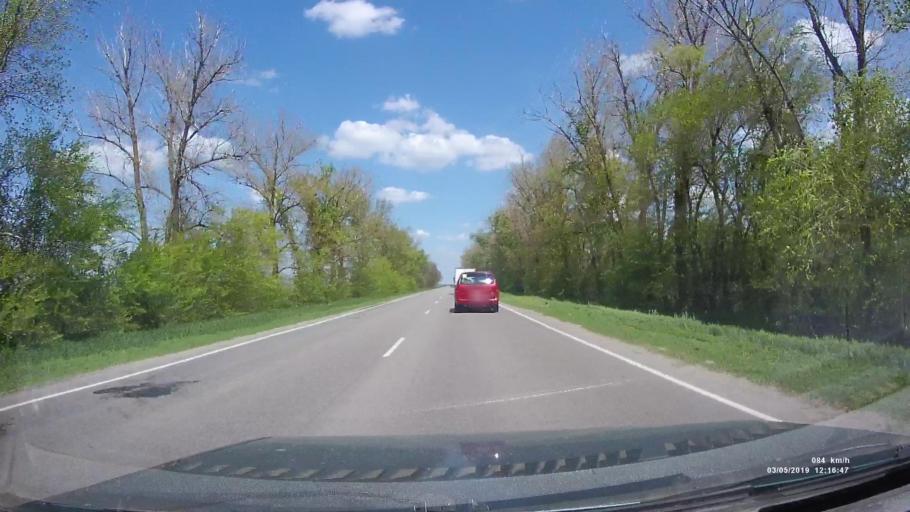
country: RU
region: Rostov
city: Melikhovskaya
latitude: 47.3763
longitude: 40.5875
